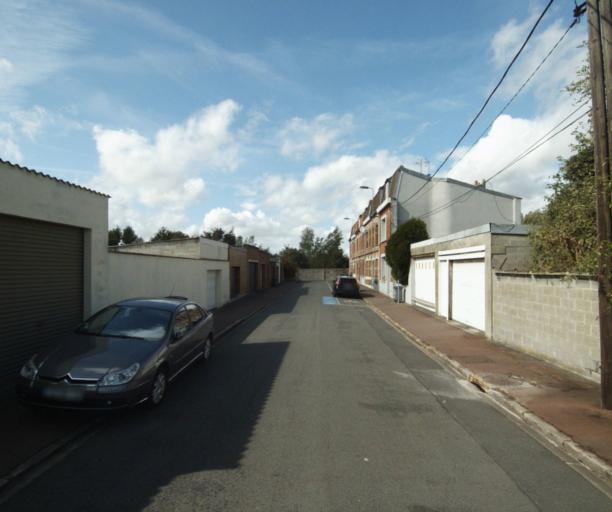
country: FR
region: Nord-Pas-de-Calais
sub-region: Departement du Nord
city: Loos
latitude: 50.6297
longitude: 3.0159
